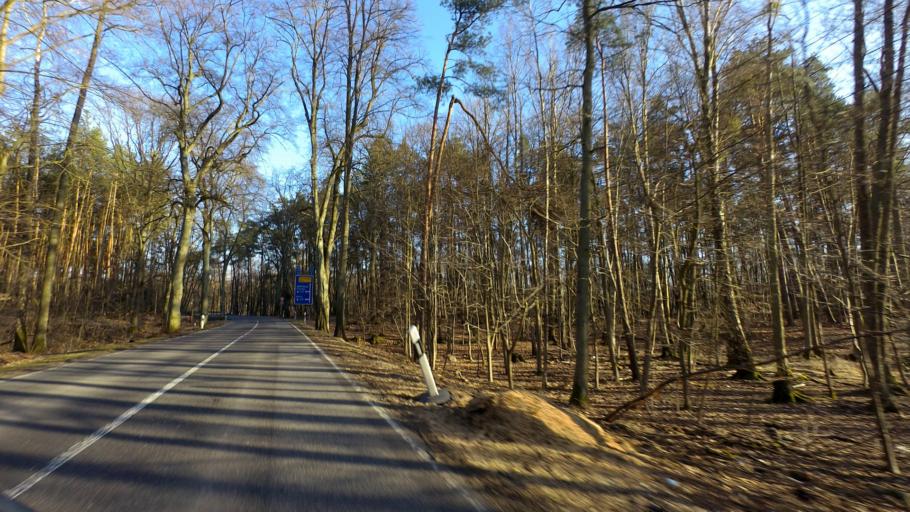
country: DE
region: Brandenburg
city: Althuttendorf
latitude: 52.9390
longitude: 13.7861
